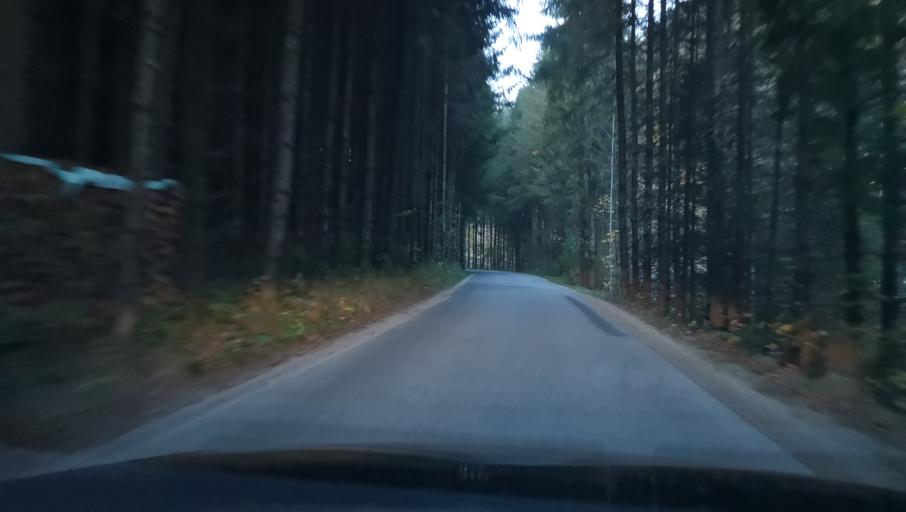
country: AT
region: Styria
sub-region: Politischer Bezirk Weiz
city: Birkfeld
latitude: 47.3391
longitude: 15.6851
